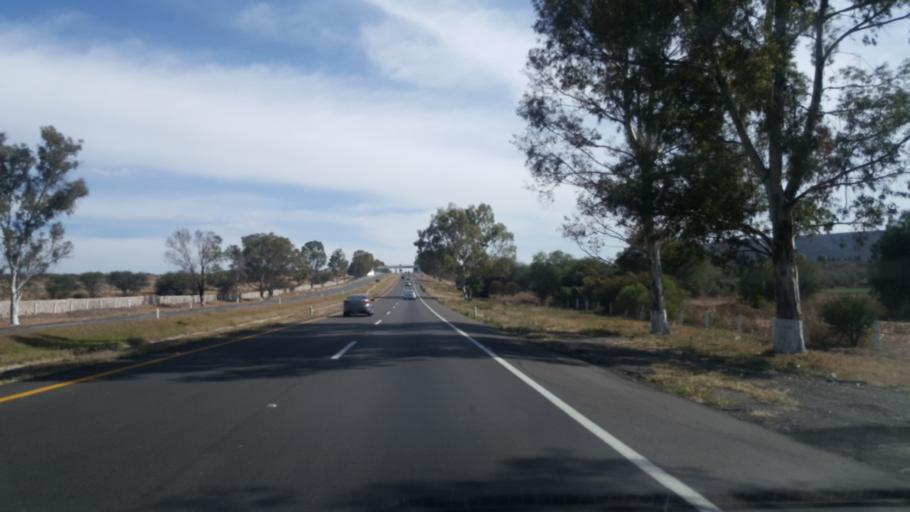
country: MX
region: Jalisco
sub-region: Lagos de Moreno
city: Cristeros [Fraccionamiento]
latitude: 21.2799
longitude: -101.9916
